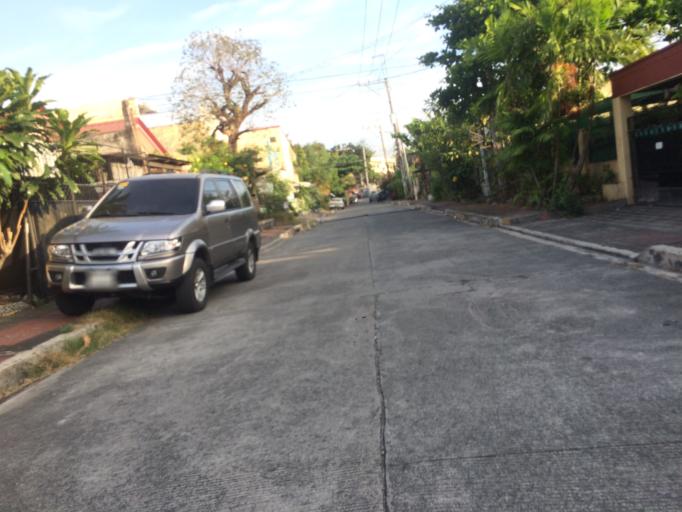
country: PH
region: Calabarzon
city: Bagong Pagasa
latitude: 14.6740
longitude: 121.0236
